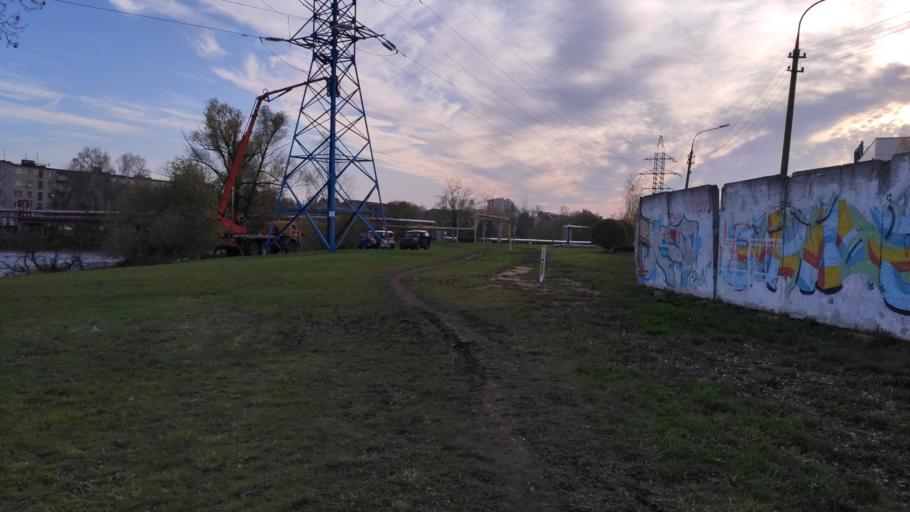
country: RU
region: Moskovskaya
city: Noginsk
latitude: 55.8720
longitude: 38.4591
